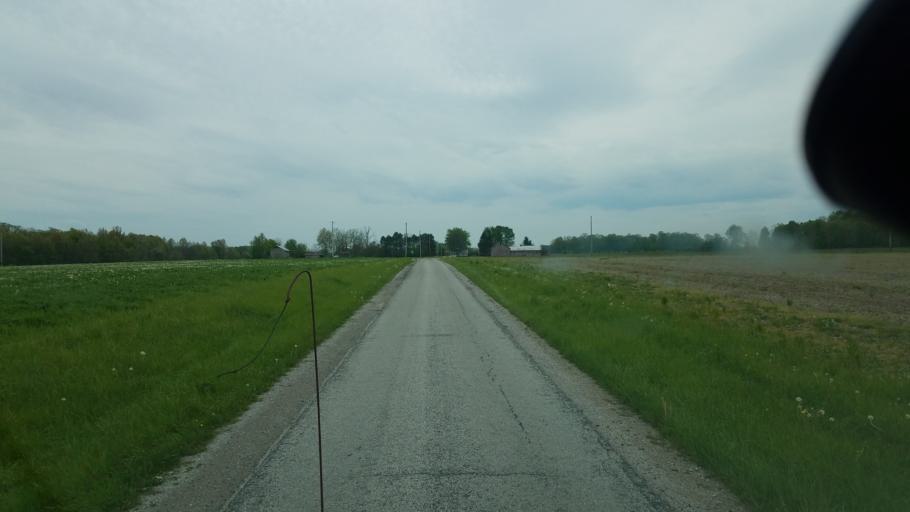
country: US
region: Ohio
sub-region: Huron County
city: Willard
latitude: 40.9977
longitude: -82.7966
